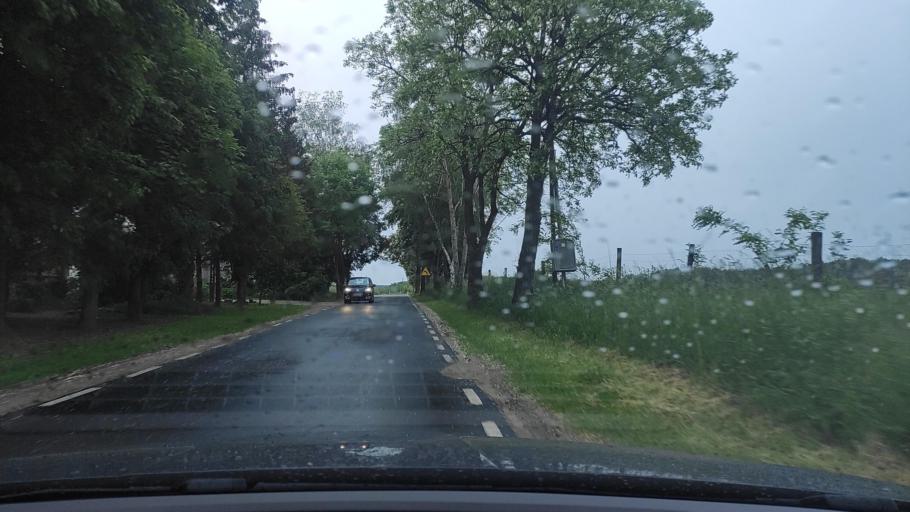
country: PL
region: Greater Poland Voivodeship
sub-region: Powiat poznanski
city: Kobylnica
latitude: 52.4840
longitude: 17.1561
